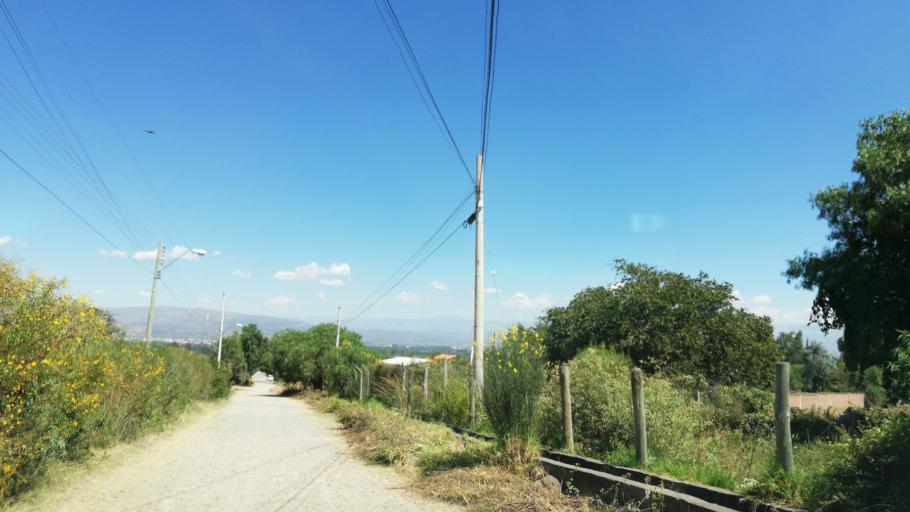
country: BO
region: Cochabamba
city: Cochabamba
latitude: -17.3271
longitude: -66.2142
